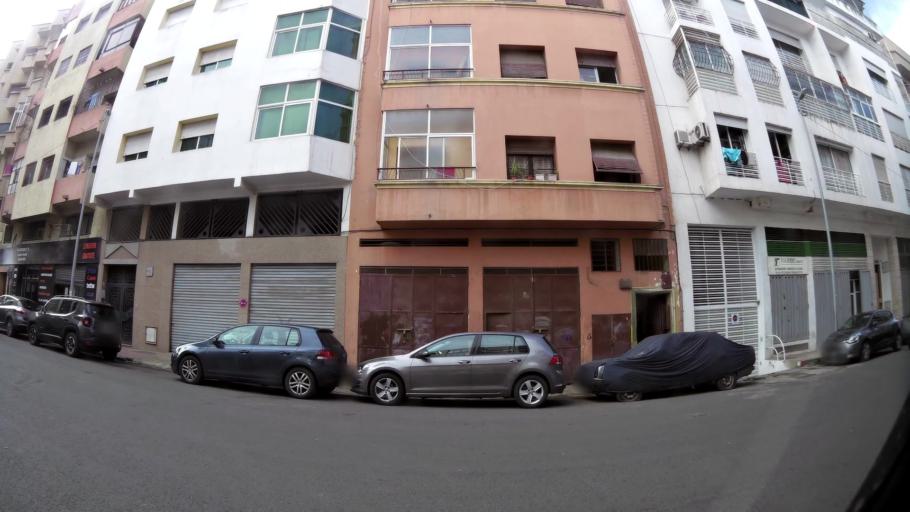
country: MA
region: Grand Casablanca
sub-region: Casablanca
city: Casablanca
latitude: 33.5952
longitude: -7.5899
